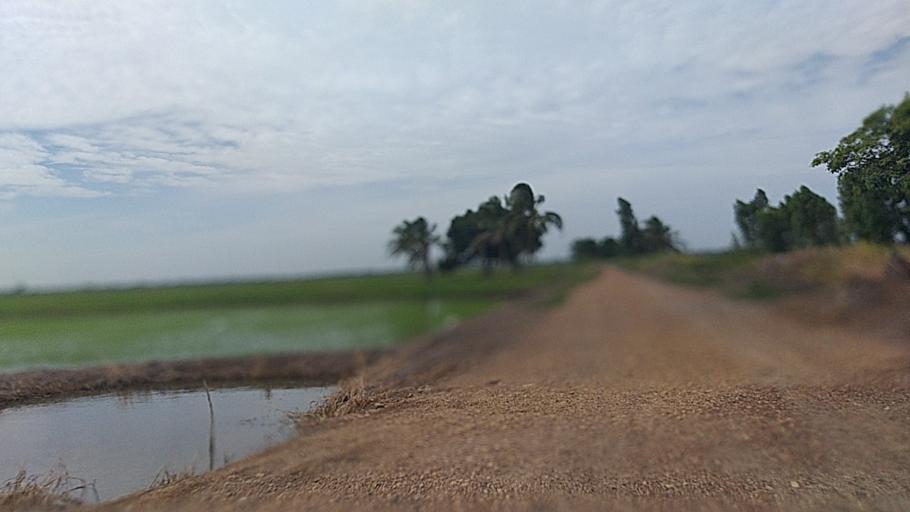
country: TH
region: Pathum Thani
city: Ban Lam Luk Ka
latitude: 14.0315
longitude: 100.8567
